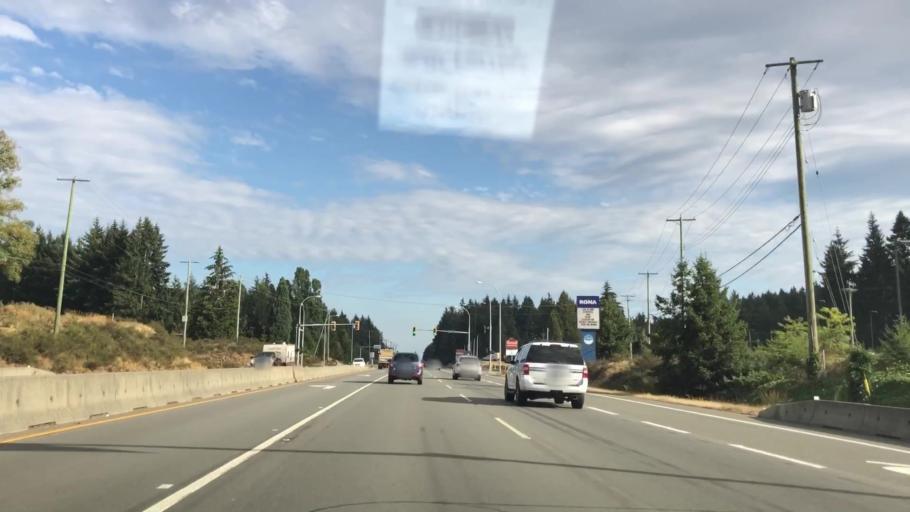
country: CA
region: British Columbia
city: Duncan
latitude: 48.6966
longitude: -123.5925
